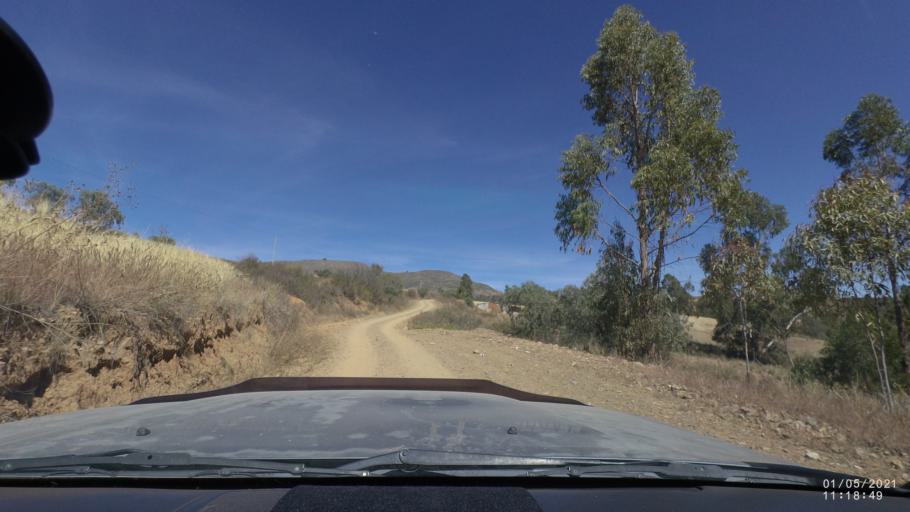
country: BO
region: Cochabamba
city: Tarata
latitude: -17.6415
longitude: -66.1187
